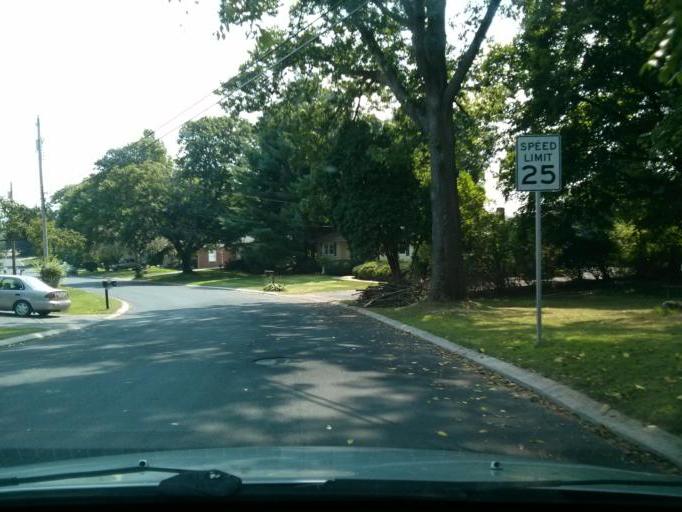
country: US
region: Pennsylvania
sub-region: Centre County
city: State College
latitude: 40.7809
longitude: -77.8768
